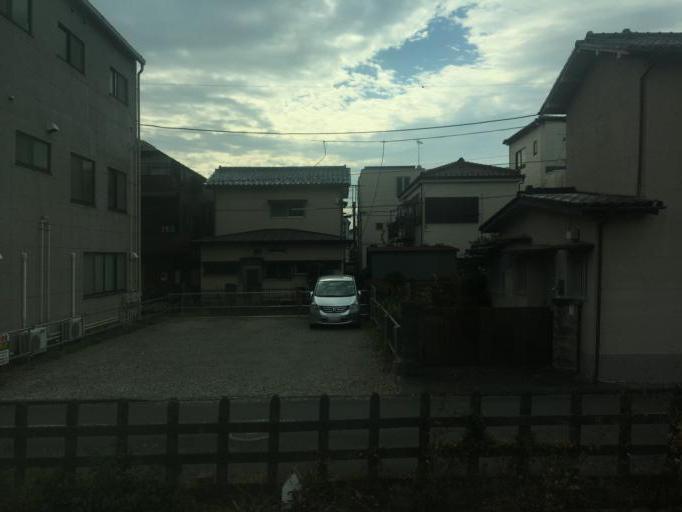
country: JP
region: Tokyo
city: Hino
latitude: 35.7073
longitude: 139.3813
